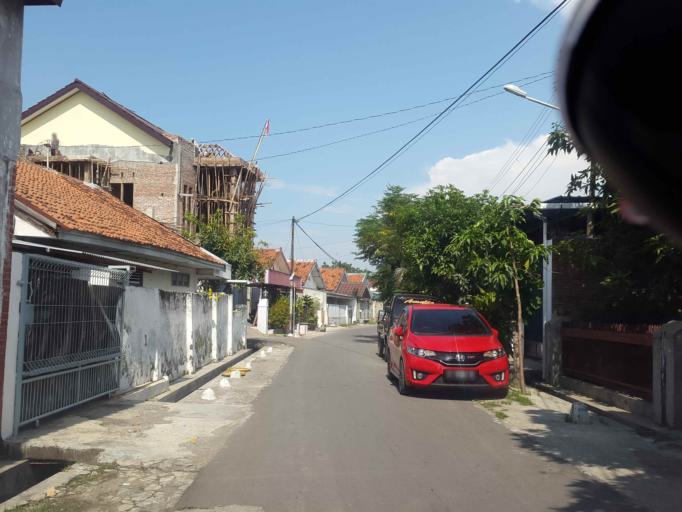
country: ID
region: Central Java
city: Tegal
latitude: -6.8568
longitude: 109.1266
